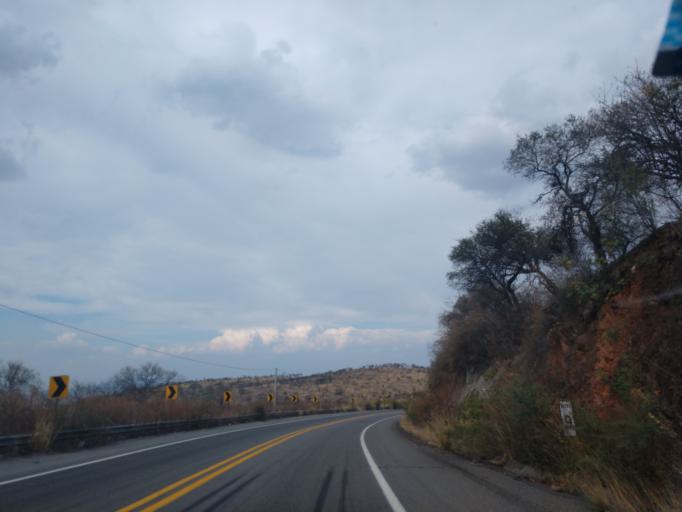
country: MX
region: Jalisco
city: La Manzanilla de la Paz
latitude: 20.1047
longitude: -103.1681
